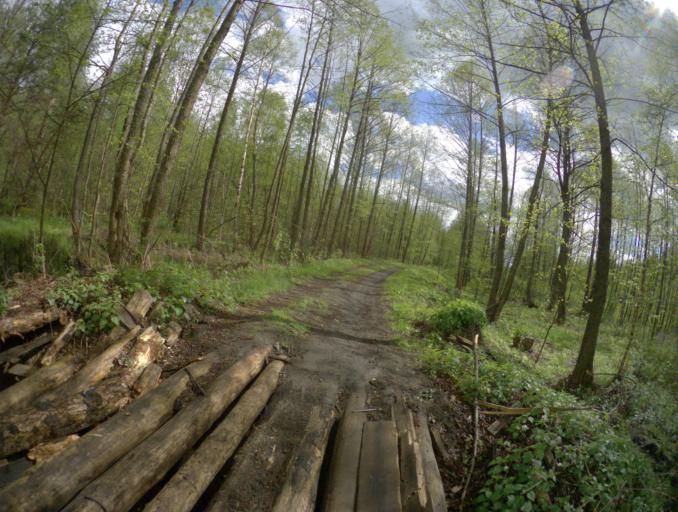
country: RU
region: Vladimir
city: Urshel'skiy
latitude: 55.5815
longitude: 40.1765
